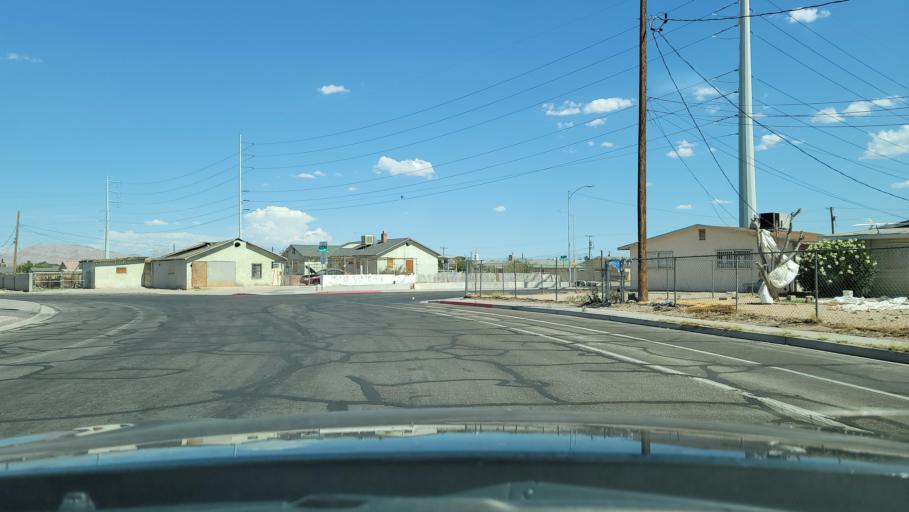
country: US
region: Nevada
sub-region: Clark County
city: Las Vegas
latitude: 36.1990
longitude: -115.1568
